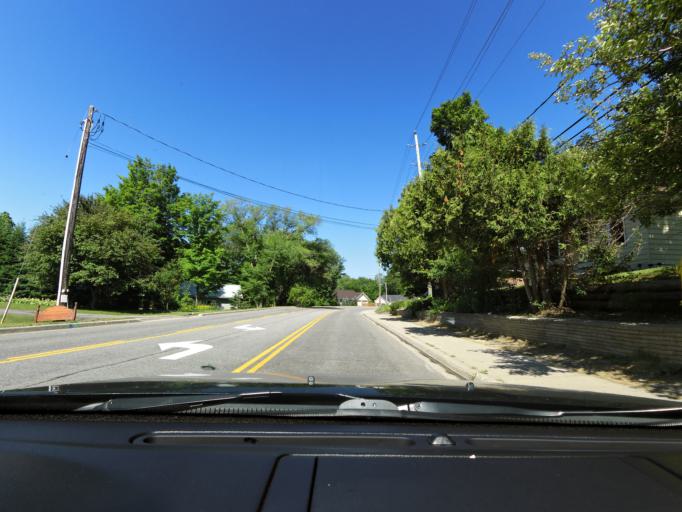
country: CA
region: Ontario
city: Huntsville
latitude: 45.3313
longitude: -79.2164
